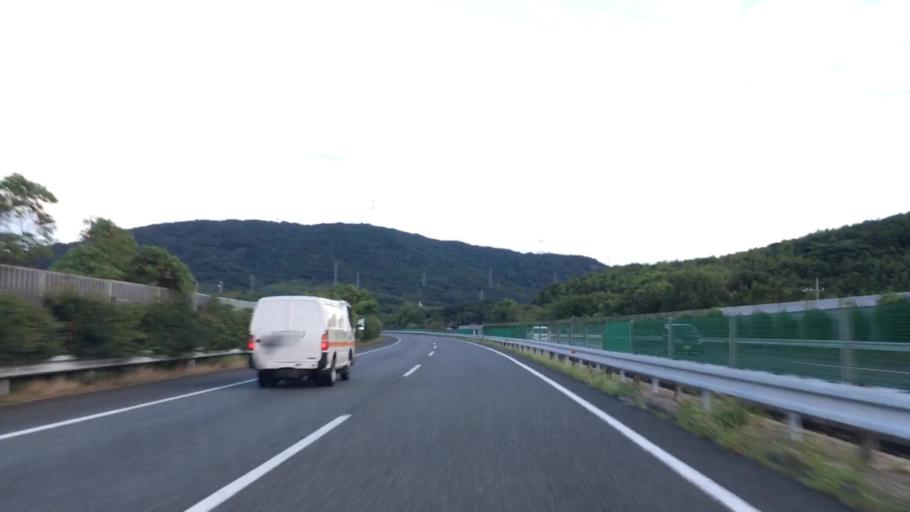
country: JP
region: Yamaguchi
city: Shimonoseki
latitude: 34.0090
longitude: 130.9559
